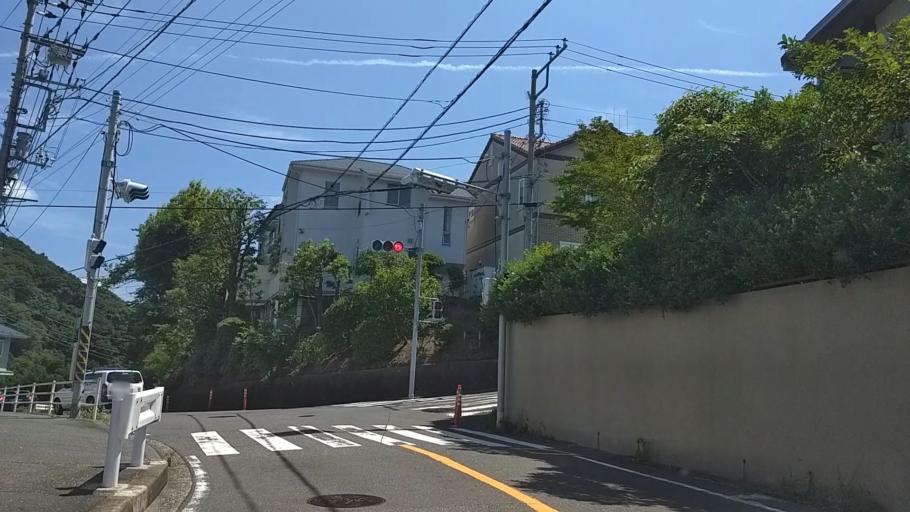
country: JP
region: Kanagawa
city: Zushi
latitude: 35.2883
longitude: 139.5914
